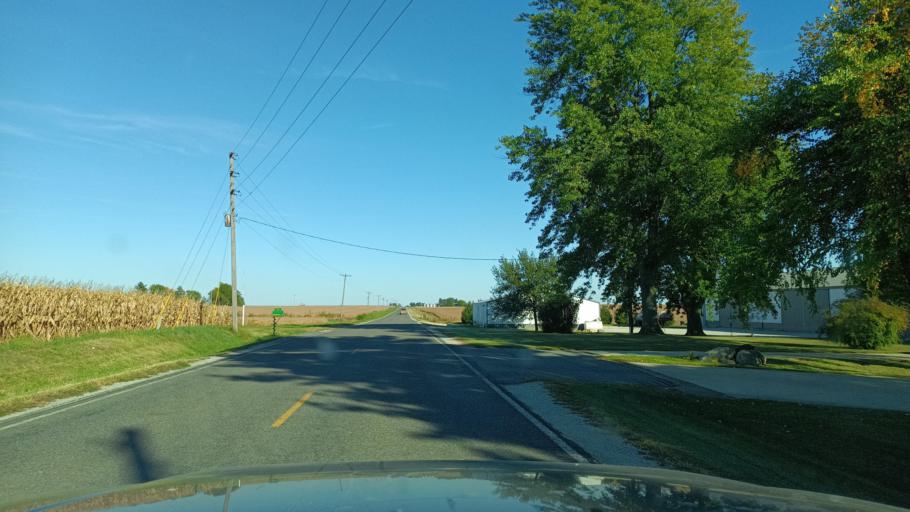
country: US
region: Illinois
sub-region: De Witt County
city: Clinton
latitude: 40.2245
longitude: -88.9050
